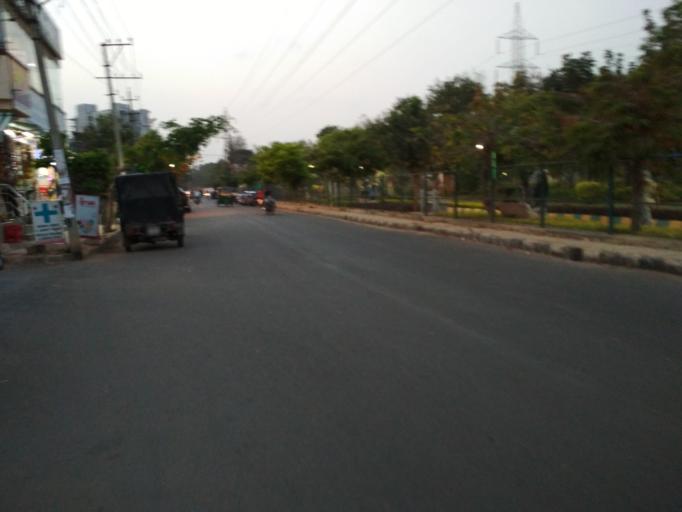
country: IN
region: Karnataka
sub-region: Bangalore Urban
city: Yelahanka
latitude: 13.0698
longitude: 77.5779
